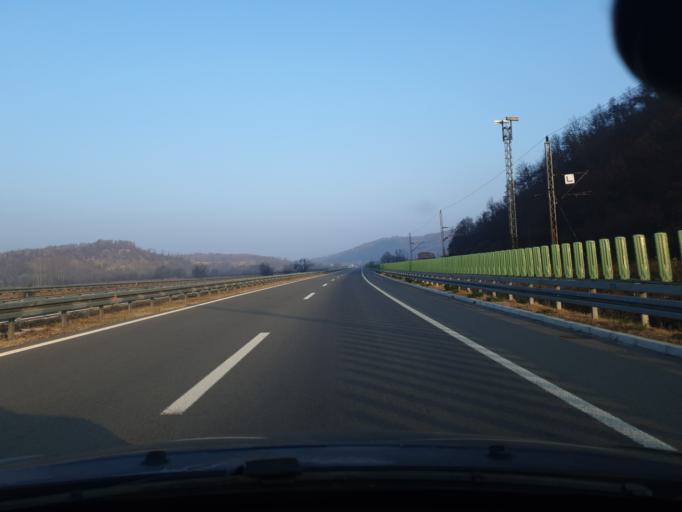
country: RS
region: Central Serbia
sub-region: Jablanicki Okrug
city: Vlasotince
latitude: 42.8984
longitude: 22.0522
